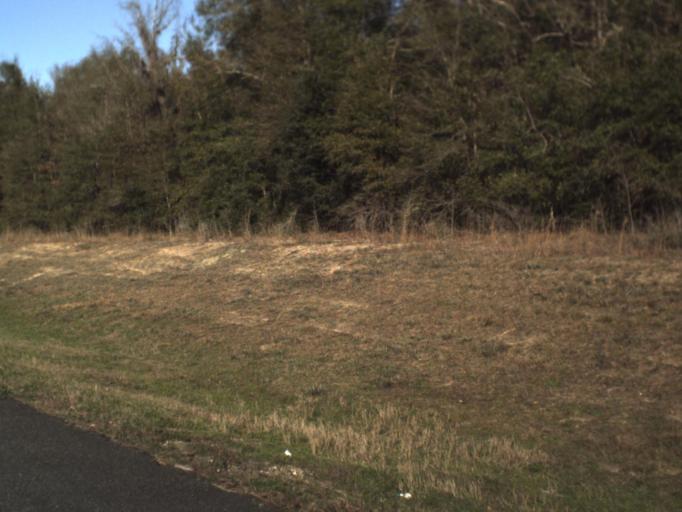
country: US
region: Florida
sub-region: Calhoun County
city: Blountstown
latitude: 30.5522
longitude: -85.1869
